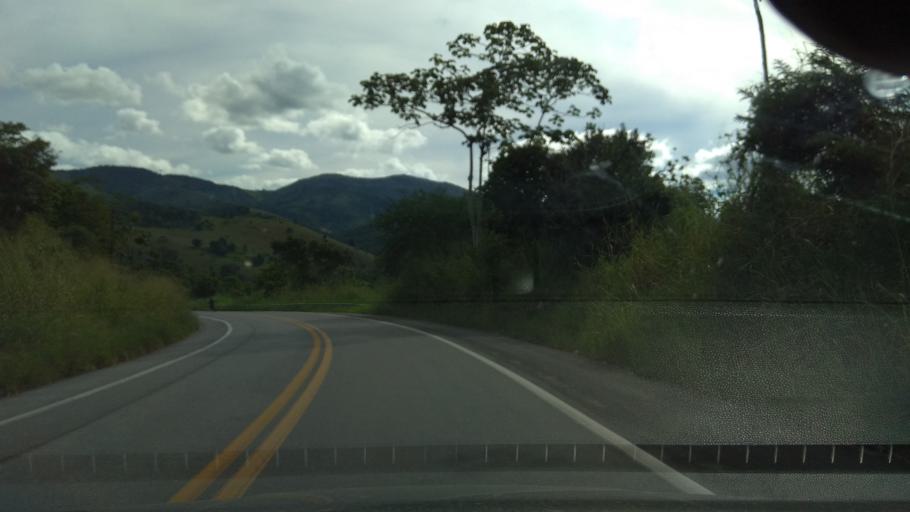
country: BR
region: Bahia
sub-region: Jitauna
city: Jitauna
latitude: -14.0074
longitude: -39.9115
